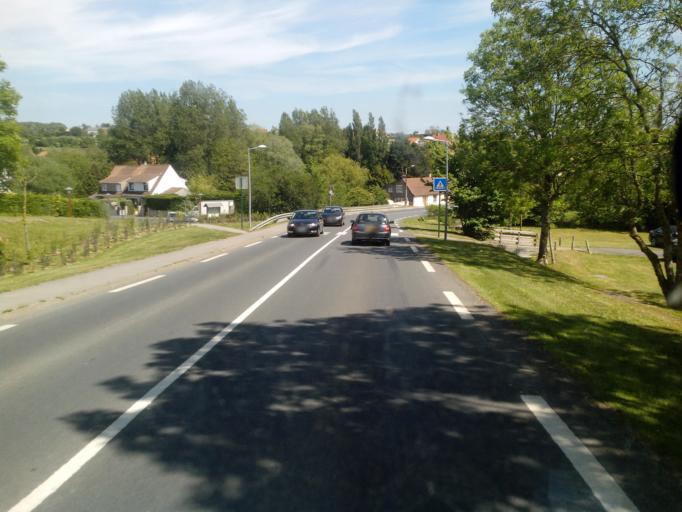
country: FR
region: Nord-Pas-de-Calais
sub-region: Departement du Pas-de-Calais
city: Isques
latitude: 50.6647
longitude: 1.6834
